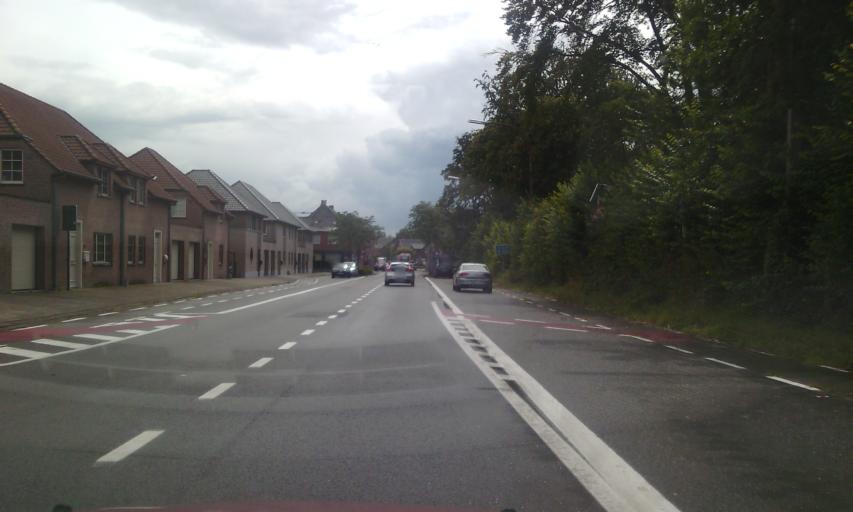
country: BE
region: Flanders
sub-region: Provincie Oost-Vlaanderen
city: Wetteren
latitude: 51.0141
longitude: 3.8808
